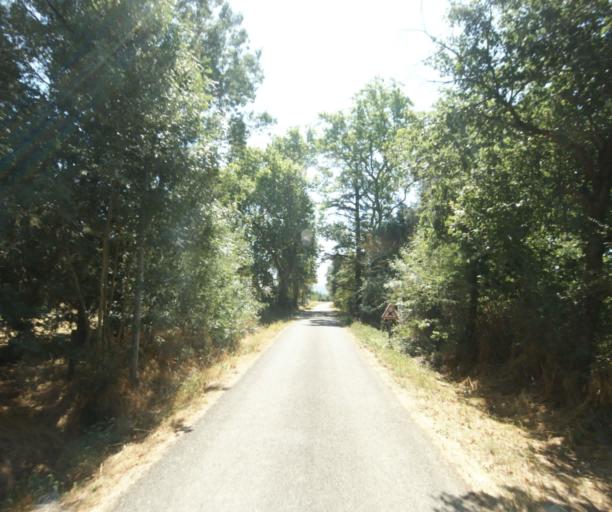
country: FR
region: Midi-Pyrenees
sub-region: Departement de la Haute-Garonne
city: Revel
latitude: 43.4820
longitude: 1.9708
